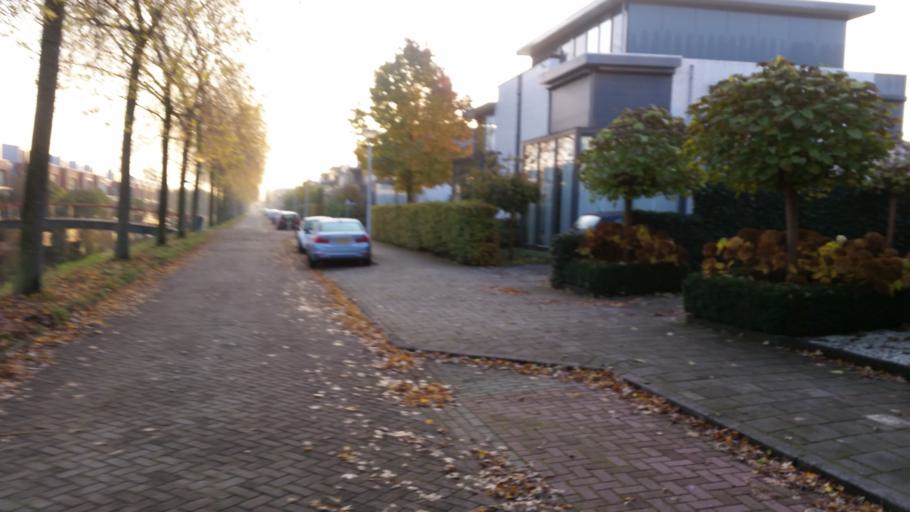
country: NL
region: North Holland
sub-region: Gemeente Ouder-Amstel
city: Ouderkerk aan de Amstel
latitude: 52.2927
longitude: 4.9096
